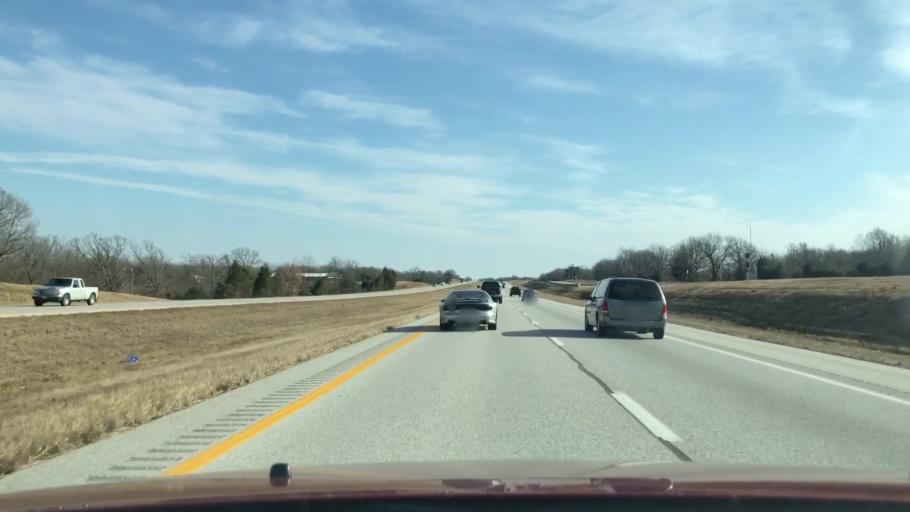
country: US
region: Missouri
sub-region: Webster County
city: Seymour
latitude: 37.1597
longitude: -92.9128
